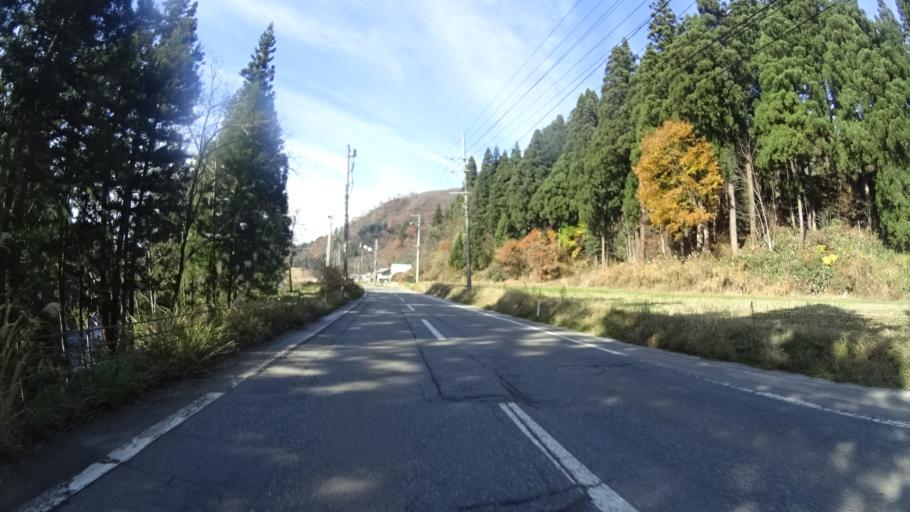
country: JP
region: Niigata
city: Muikamachi
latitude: 37.2225
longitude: 139.0264
